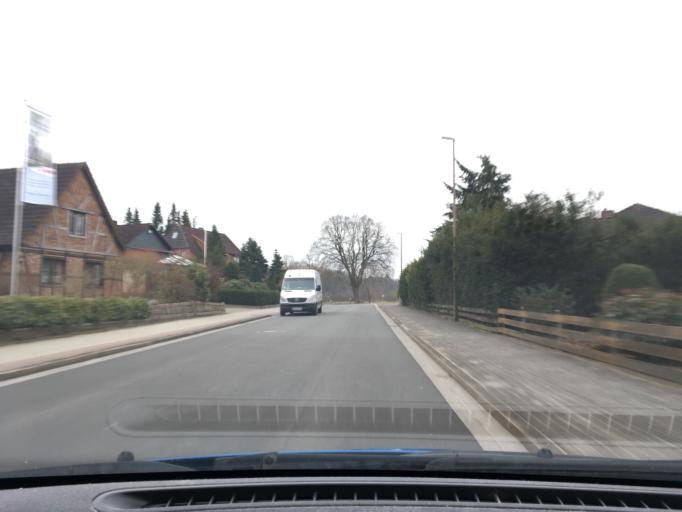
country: DE
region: Lower Saxony
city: Vogelsen
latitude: 53.2693
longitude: 10.3625
